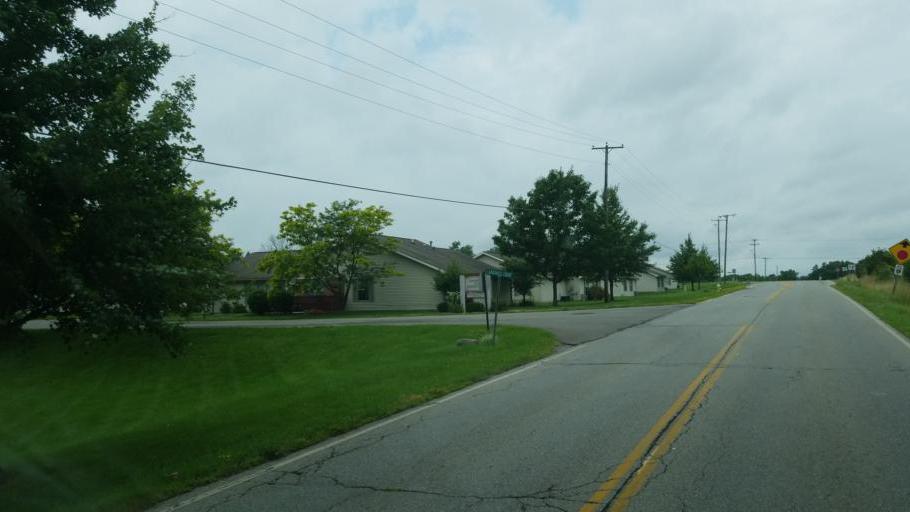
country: US
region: Ohio
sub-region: Richland County
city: Ontario
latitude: 40.7842
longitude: -82.5708
